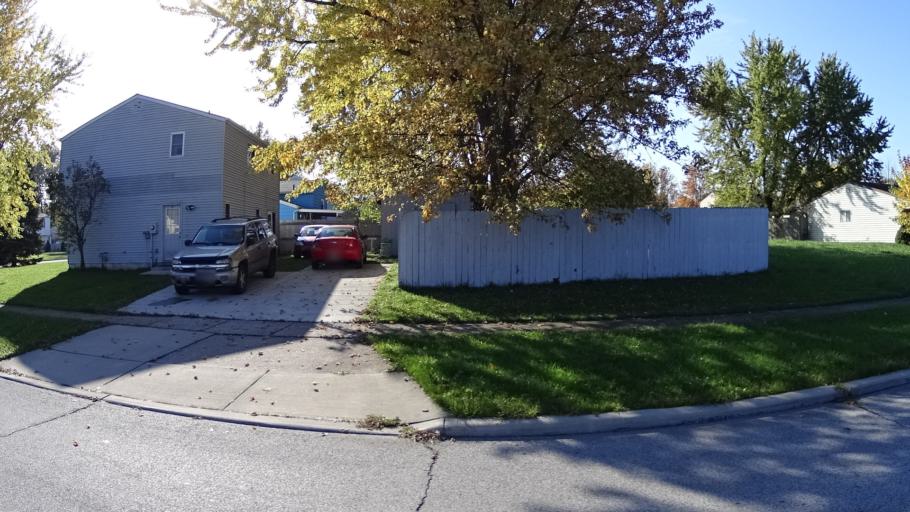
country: US
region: Ohio
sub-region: Lorain County
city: Lorain
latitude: 41.4687
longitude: -82.1478
